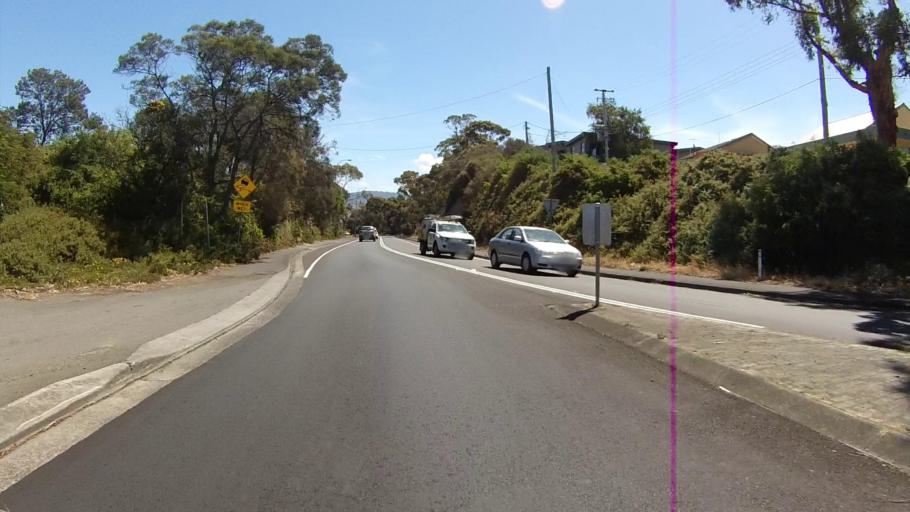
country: AU
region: Tasmania
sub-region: Sorell
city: Sorell
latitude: -42.8040
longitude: 147.5326
